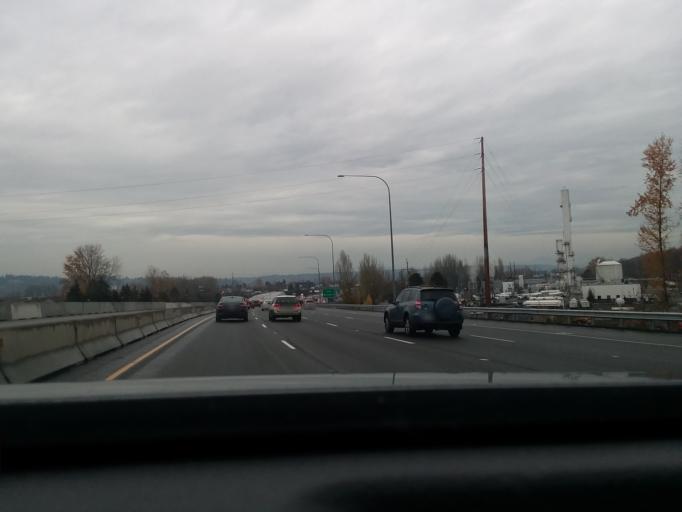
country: US
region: Washington
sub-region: Pierce County
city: Fife
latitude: 47.2414
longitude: -122.3951
